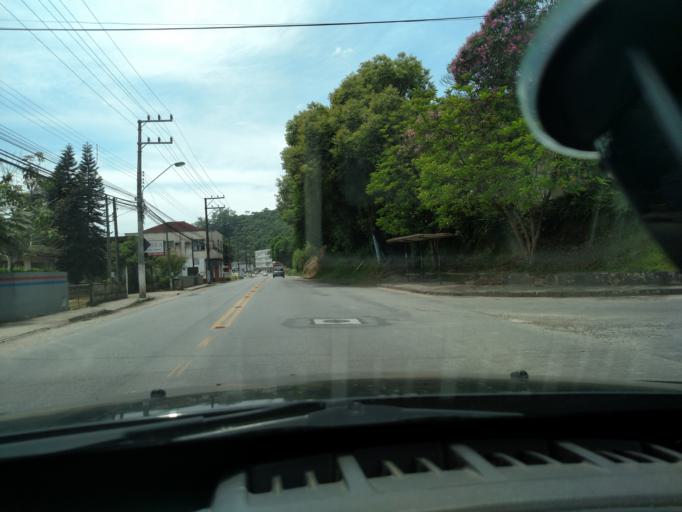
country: BR
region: Santa Catarina
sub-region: Blumenau
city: Blumenau
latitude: -26.9124
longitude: -49.0497
